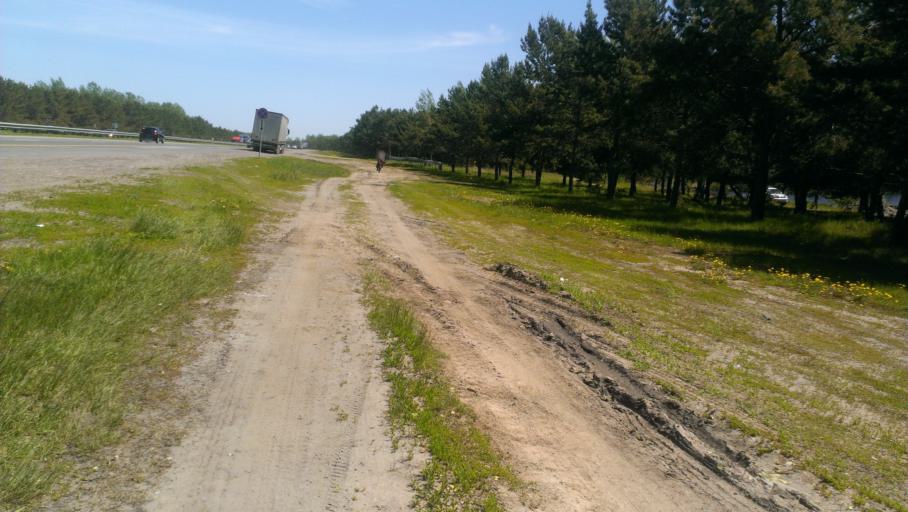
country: RU
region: Altai Krai
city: Zaton
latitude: 53.3150
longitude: 83.8487
